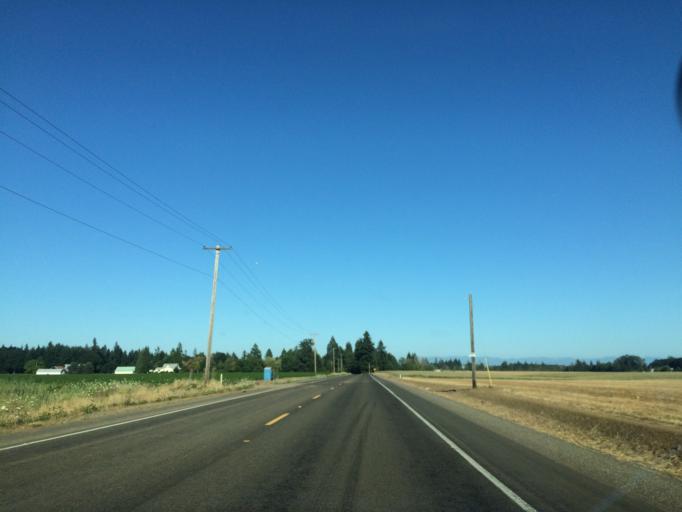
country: US
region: Oregon
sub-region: Marion County
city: Hubbard
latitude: 45.2281
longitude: -122.8739
